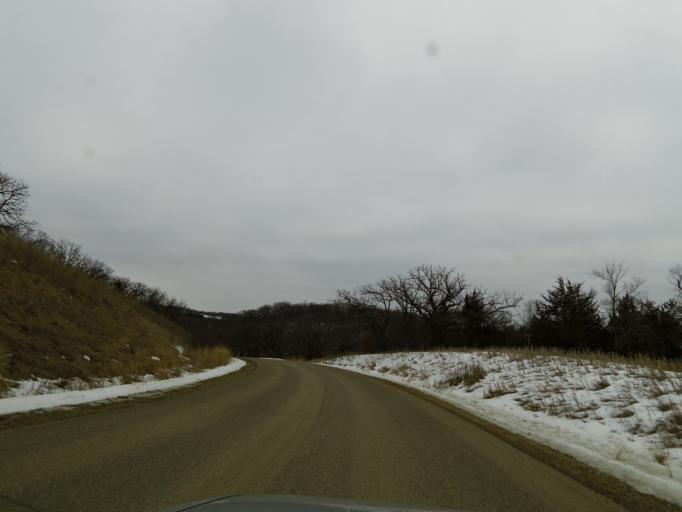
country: US
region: Minnesota
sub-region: Washington County
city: Afton
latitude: 44.8452
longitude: -92.7926
